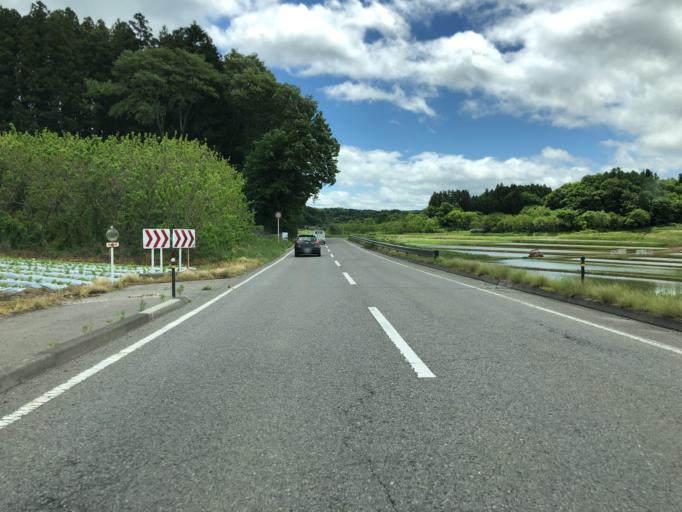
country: JP
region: Fukushima
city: Motomiya
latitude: 37.5175
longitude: 140.4693
